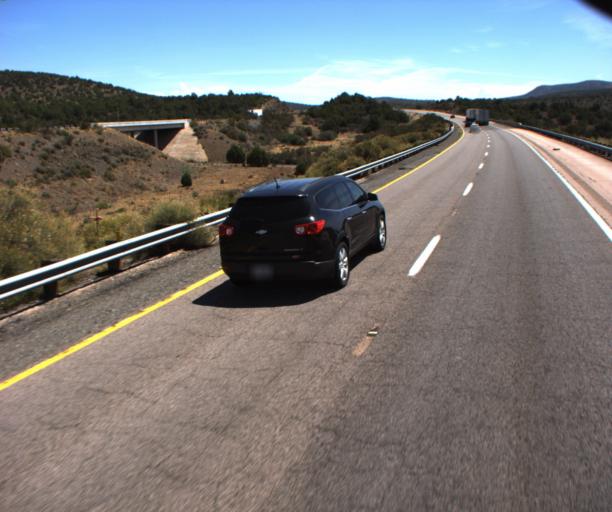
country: US
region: Arizona
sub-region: Mohave County
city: Peach Springs
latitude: 35.1890
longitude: -113.3183
